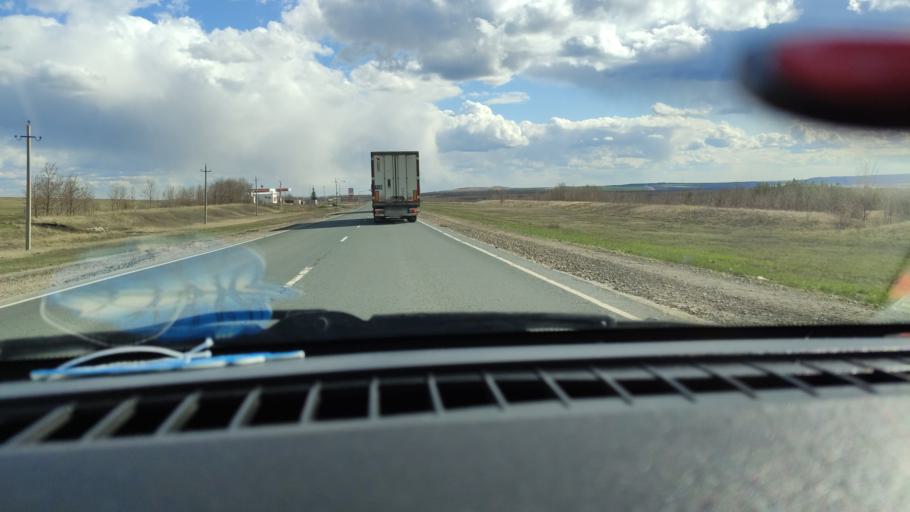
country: RU
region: Saratov
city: Alekseyevka
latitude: 52.2926
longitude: 47.9292
